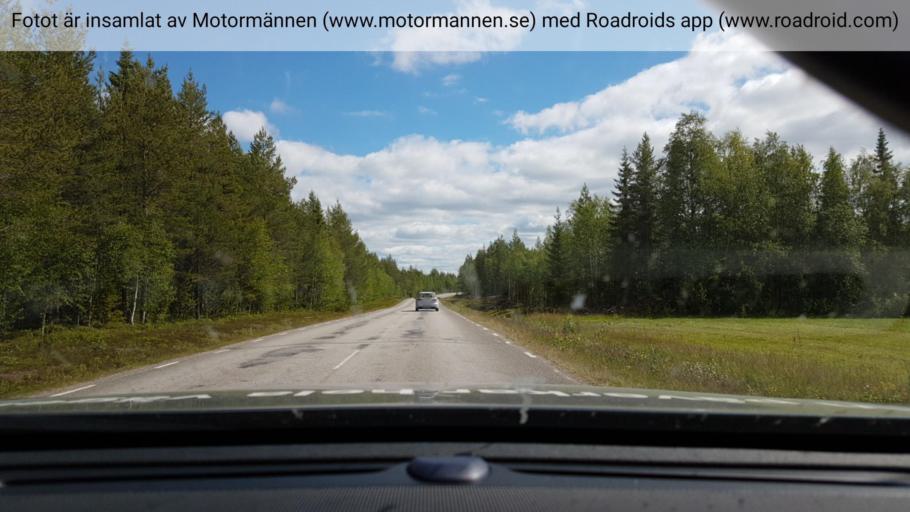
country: SE
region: Vaesterbotten
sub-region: Sorsele Kommun
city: Sorsele
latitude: 65.5943
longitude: 17.5035
